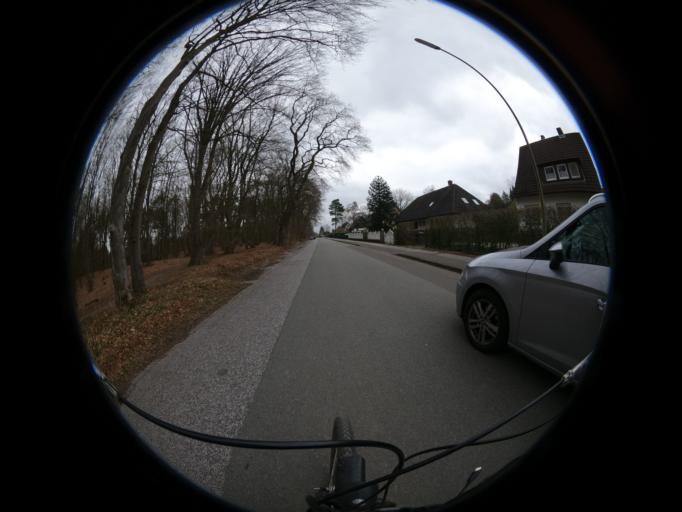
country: DE
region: Lower Saxony
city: Neu Wulmstorf
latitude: 53.4582
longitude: 9.8509
